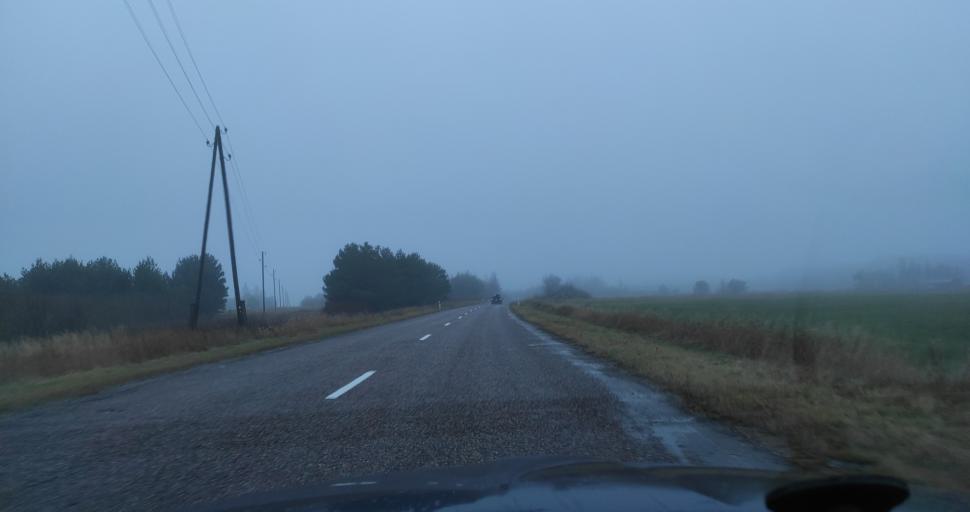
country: LV
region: Alsunga
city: Alsunga
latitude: 57.1186
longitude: 21.4245
